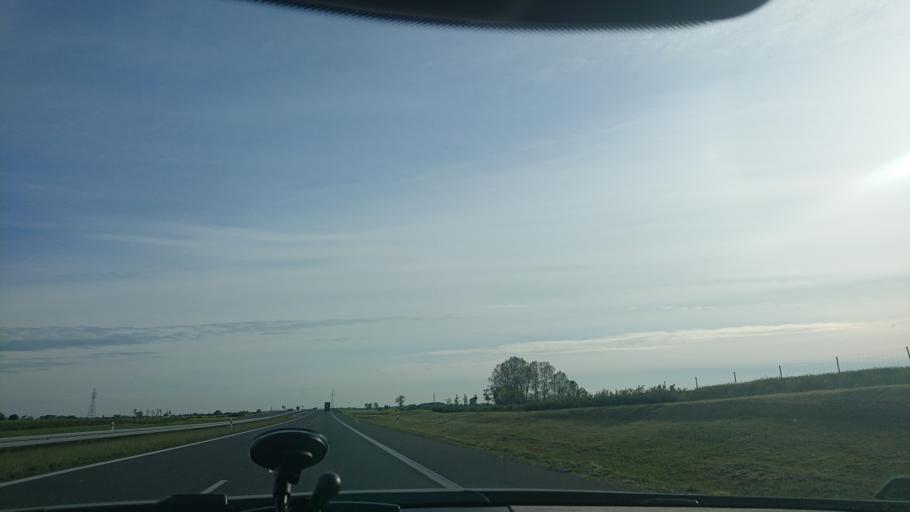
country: PL
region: Greater Poland Voivodeship
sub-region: Powiat gnieznienski
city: Gniezno
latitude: 52.5368
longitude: 17.5217
